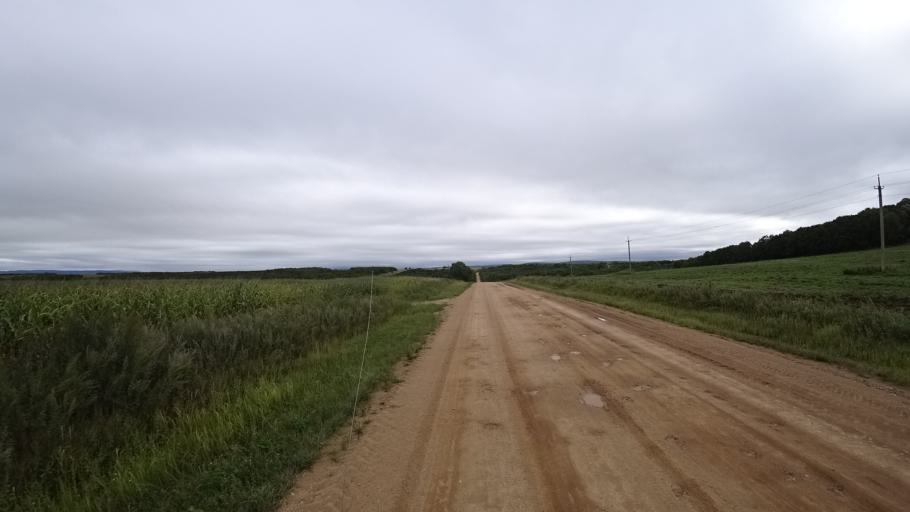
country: RU
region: Primorskiy
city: Monastyrishche
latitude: 44.0912
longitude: 132.5988
